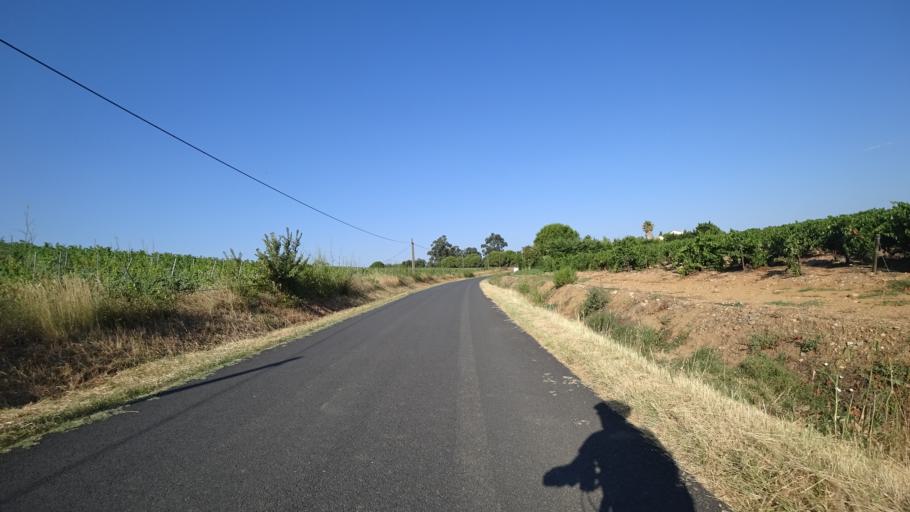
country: FR
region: Languedoc-Roussillon
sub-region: Departement des Pyrenees-Orientales
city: Villelongue-de-la-Salanque
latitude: 42.6968
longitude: 2.9826
